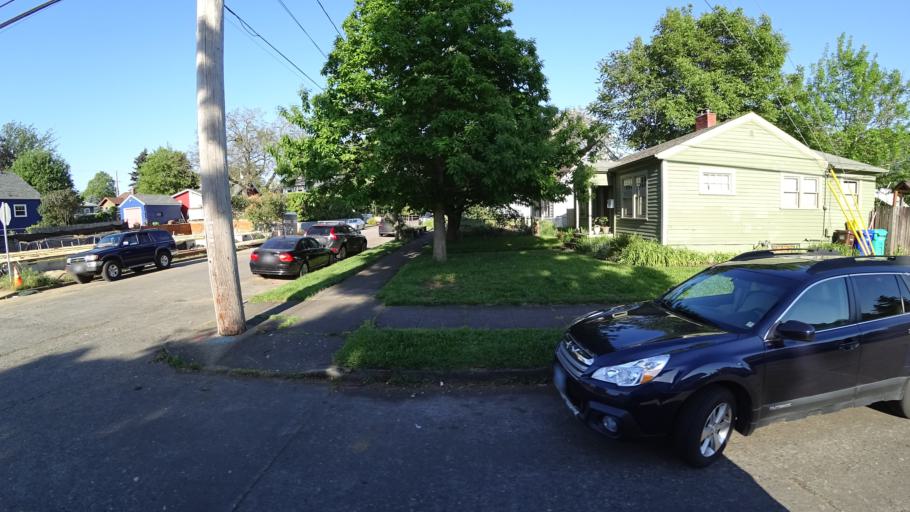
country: US
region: Oregon
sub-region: Multnomah County
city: Portland
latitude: 45.5582
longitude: -122.6811
